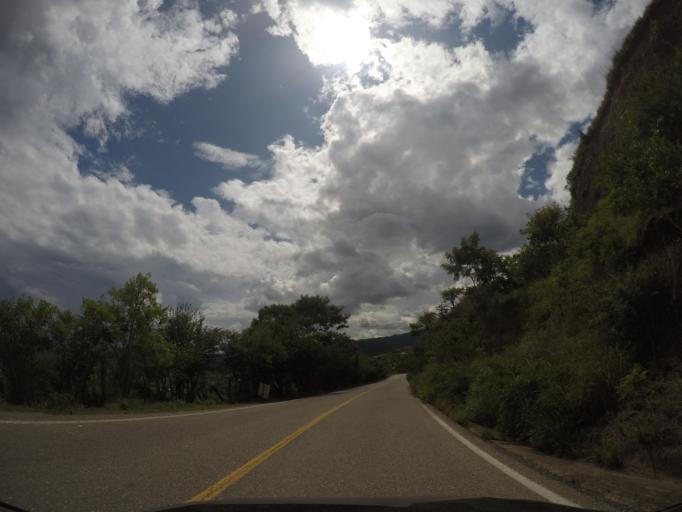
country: MX
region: Oaxaca
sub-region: San Jeronimo Coatlan
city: San Cristobal Honduras
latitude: 16.4330
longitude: -97.0597
